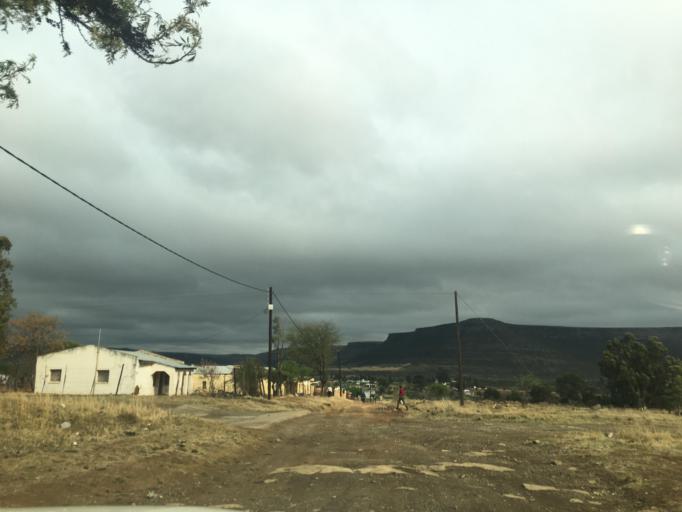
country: ZA
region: Eastern Cape
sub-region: Chris Hani District Municipality
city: Cala
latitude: -31.5227
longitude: 27.6918
